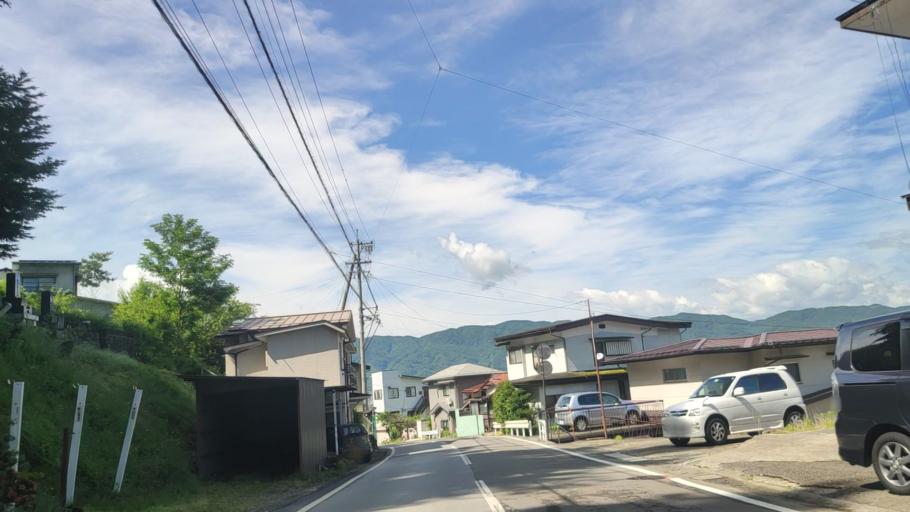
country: JP
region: Nagano
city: Suwa
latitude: 36.0421
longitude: 138.1265
